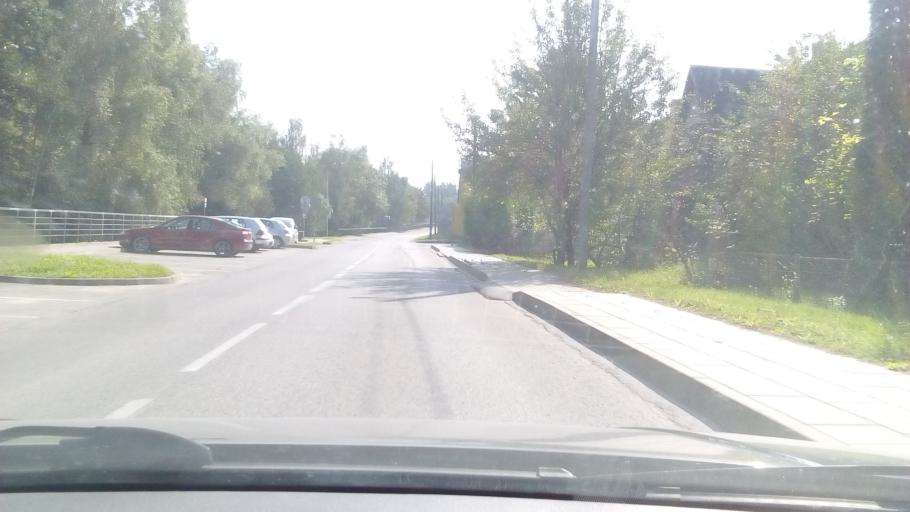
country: LT
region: Alytaus apskritis
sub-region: Alytus
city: Alytus
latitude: 54.3906
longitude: 24.0605
